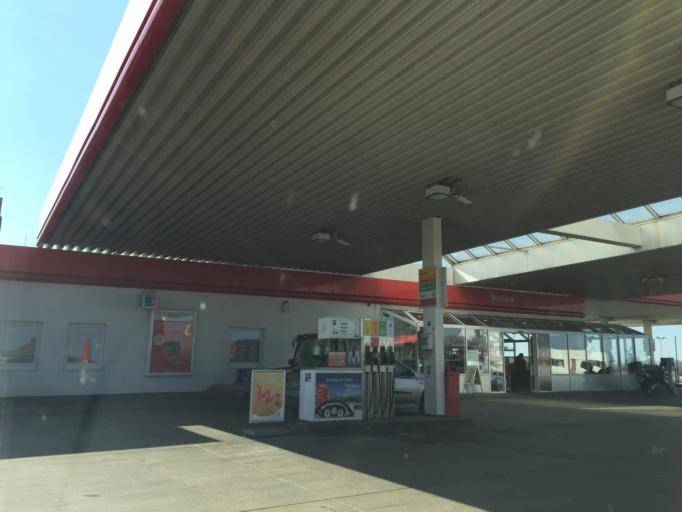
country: DE
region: Thuringia
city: Waltershausen
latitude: 50.9224
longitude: 10.5525
